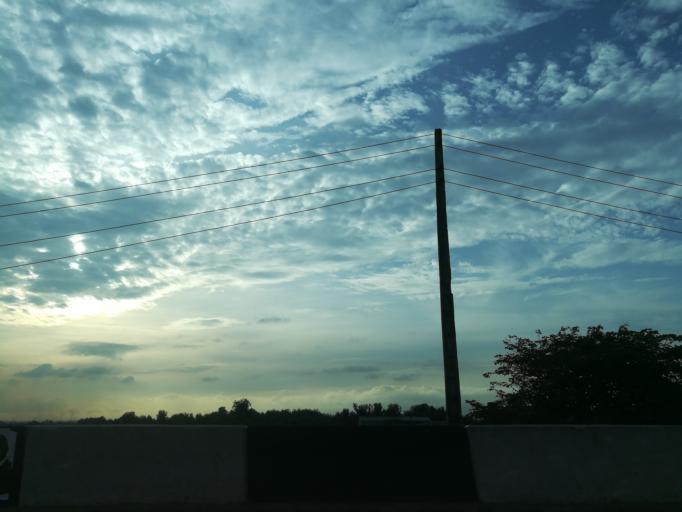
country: NG
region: Lagos
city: Ebute Ikorodu
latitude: 6.6110
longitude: 3.4407
